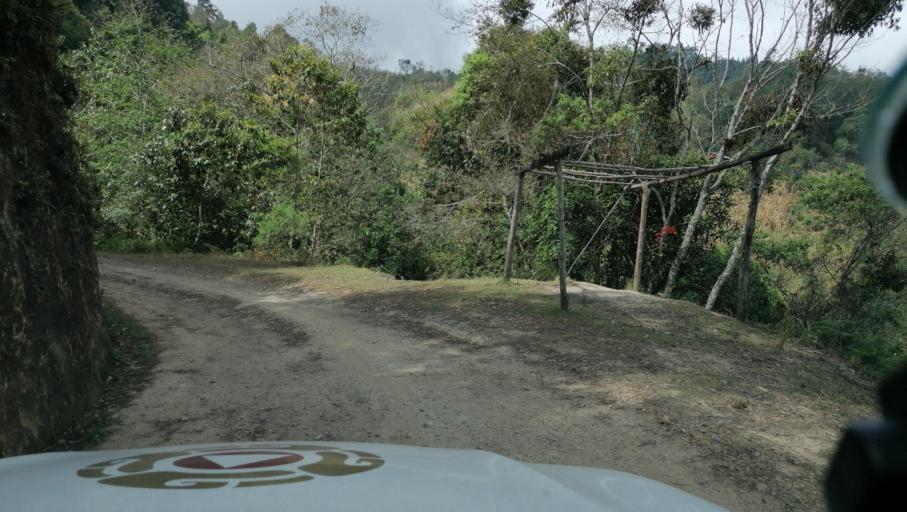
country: MX
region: Chiapas
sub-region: Cacahoatan
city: Benito Juarez
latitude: 15.2005
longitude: -92.2236
